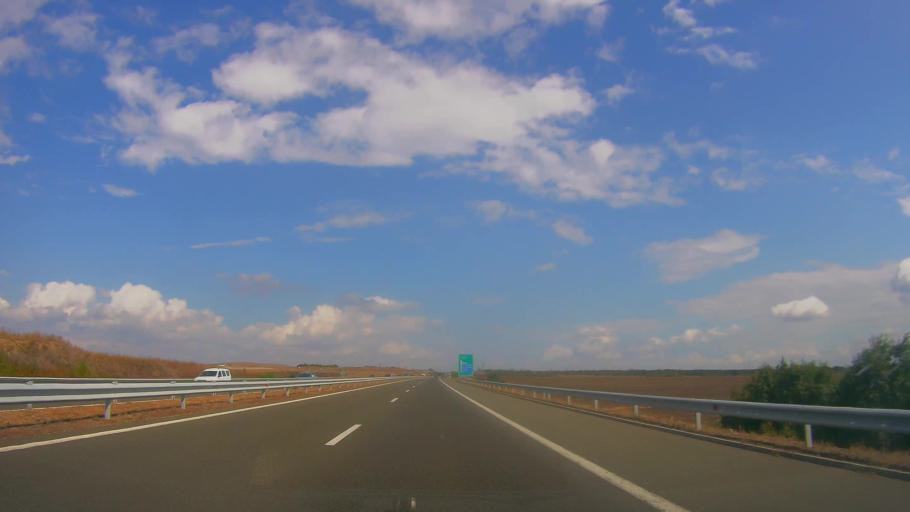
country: BG
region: Burgas
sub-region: Obshtina Karnobat
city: Karnobat
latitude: 42.5895
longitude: 26.9738
